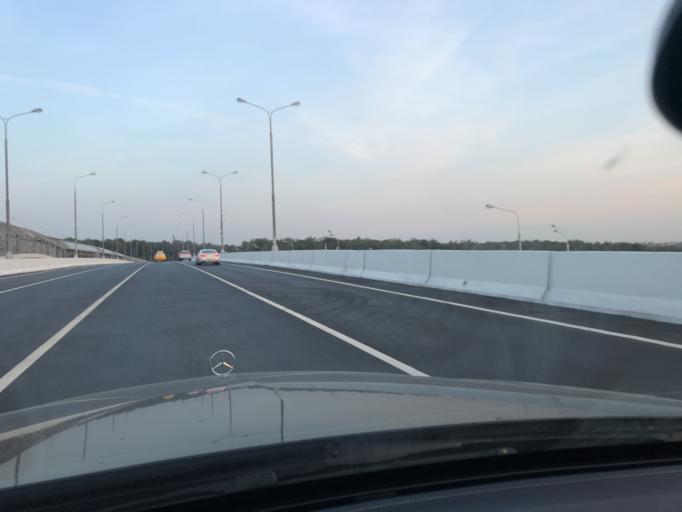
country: RU
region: Moskovskaya
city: Mosrentgen
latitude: 55.5843
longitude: 37.4384
